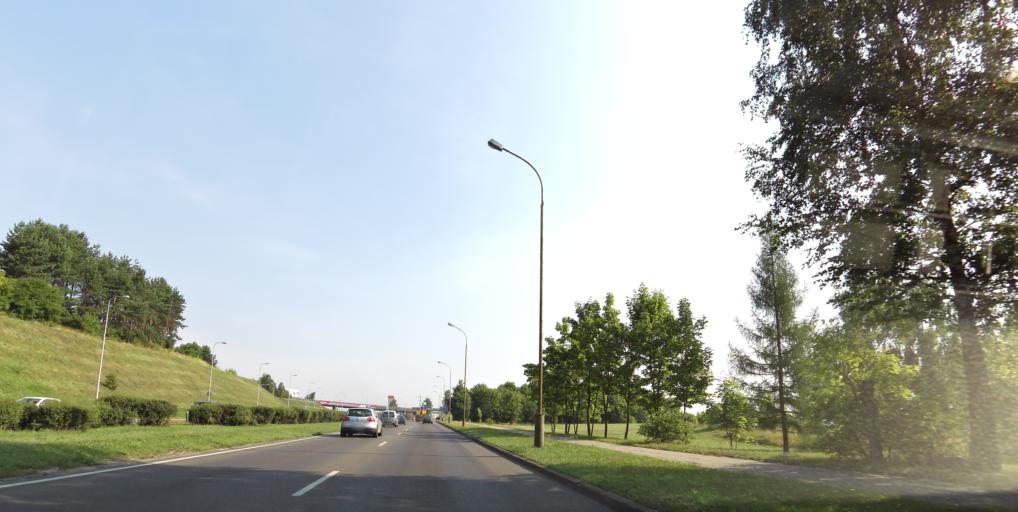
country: LT
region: Vilnius County
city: Seskine
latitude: 54.7096
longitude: 25.2691
